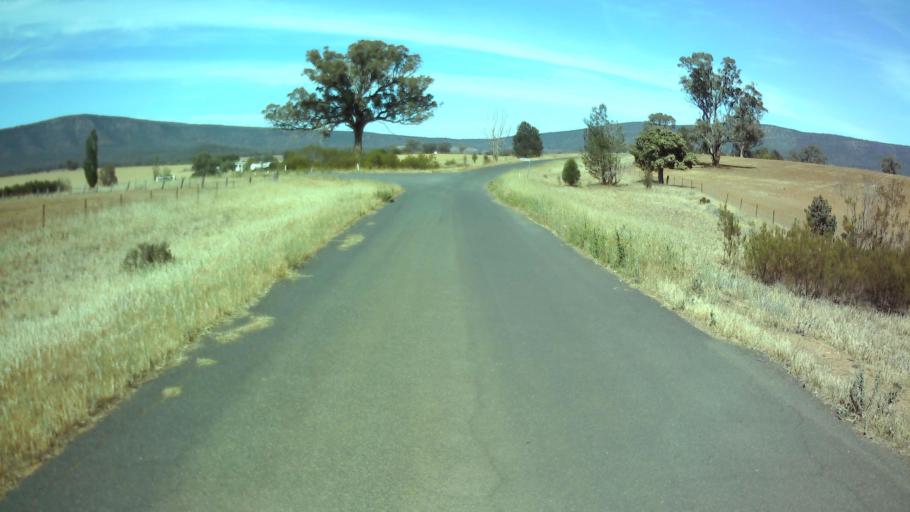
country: AU
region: New South Wales
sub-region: Weddin
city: Grenfell
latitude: -33.9407
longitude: 148.0682
